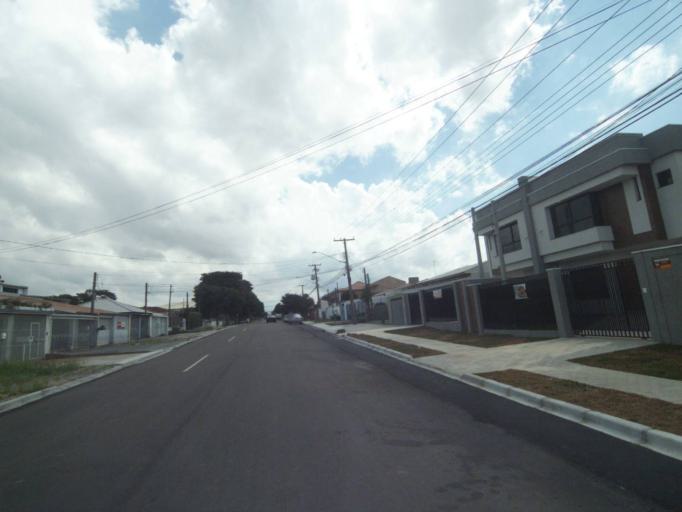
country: BR
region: Parana
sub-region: Pinhais
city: Pinhais
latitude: -25.4611
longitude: -49.2080
